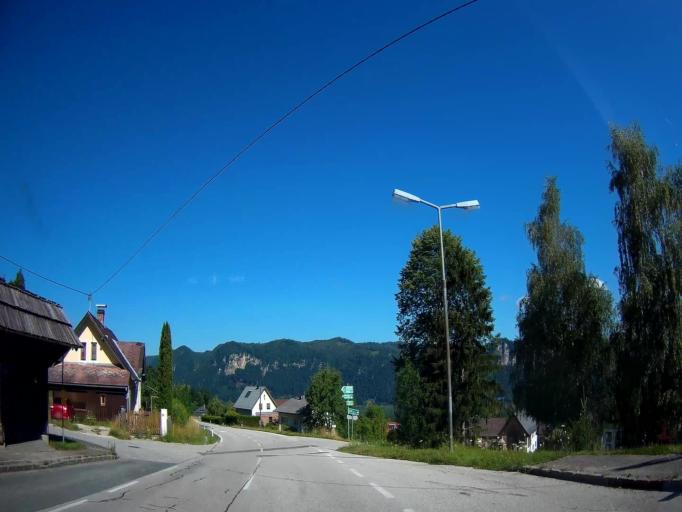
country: AT
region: Carinthia
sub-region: Politischer Bezirk Klagenfurt Land
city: Ebenthal
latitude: 46.5360
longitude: 14.3999
